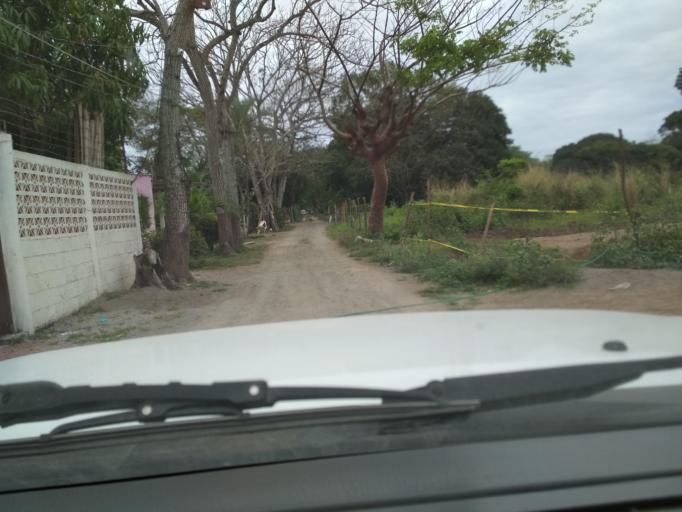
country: MX
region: Veracruz
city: El Tejar
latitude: 19.0719
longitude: -96.1409
